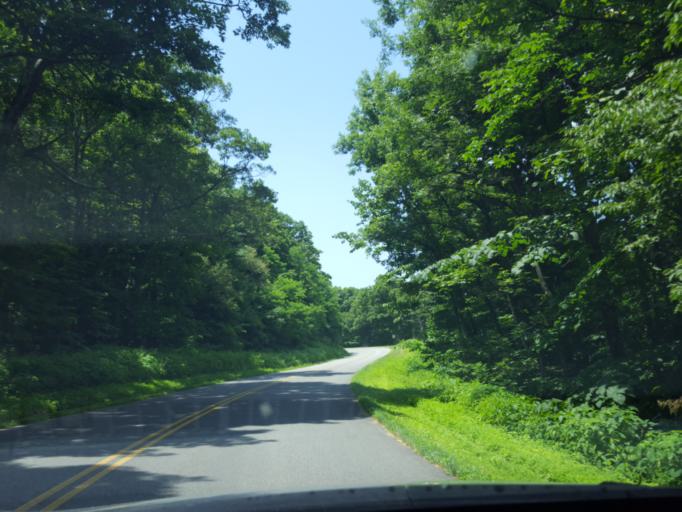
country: US
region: Virginia
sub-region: Nelson County
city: Nellysford
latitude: 37.9403
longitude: -78.9336
